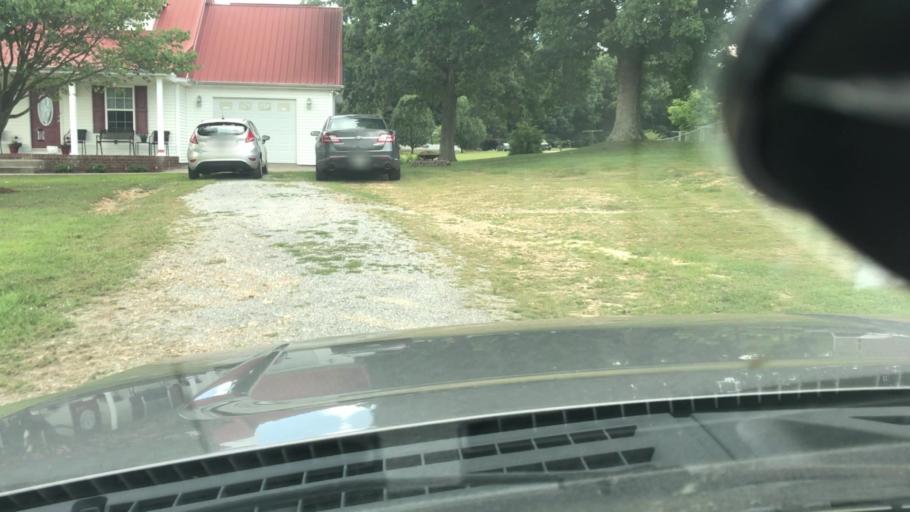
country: US
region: Tennessee
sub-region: Sumner County
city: Westmoreland
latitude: 36.5957
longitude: -86.3626
